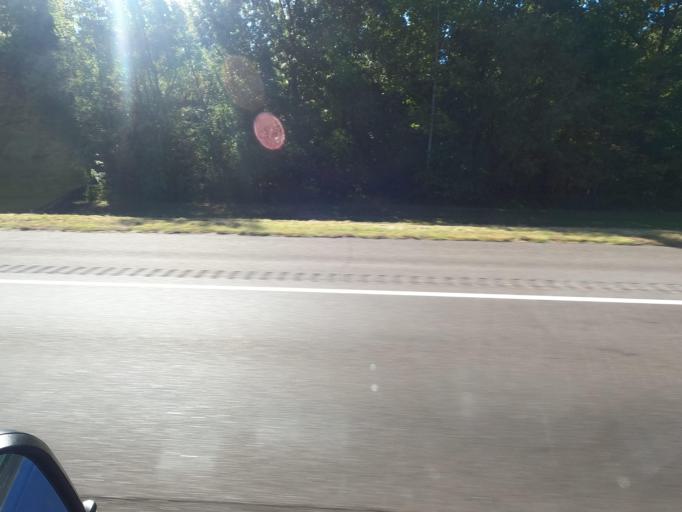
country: US
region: Tennessee
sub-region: Obion County
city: Obion
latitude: 36.2286
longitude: -89.2133
